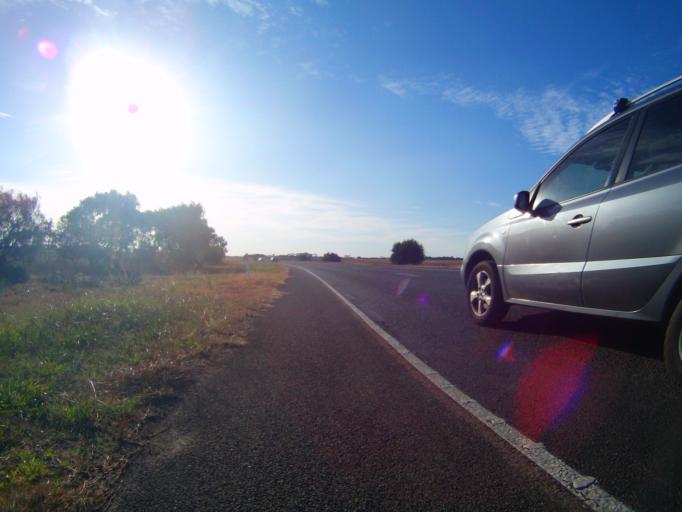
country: AU
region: Victoria
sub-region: Greater Geelong
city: Leopold
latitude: -38.2626
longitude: 144.4362
